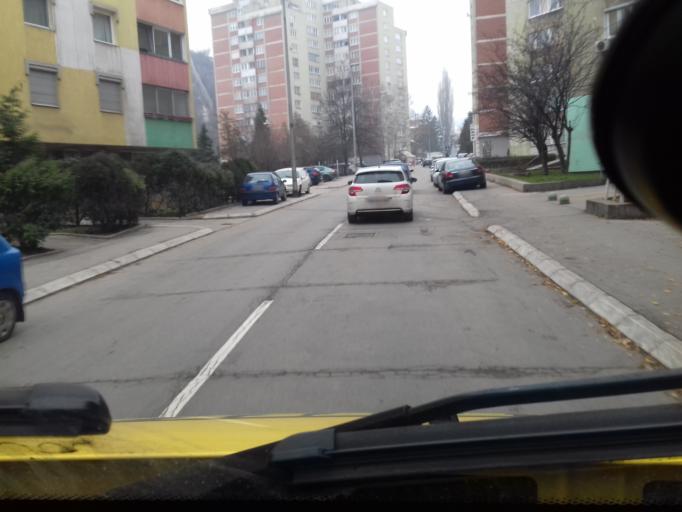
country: BA
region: Federation of Bosnia and Herzegovina
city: Zenica
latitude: 44.1941
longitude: 17.9104
